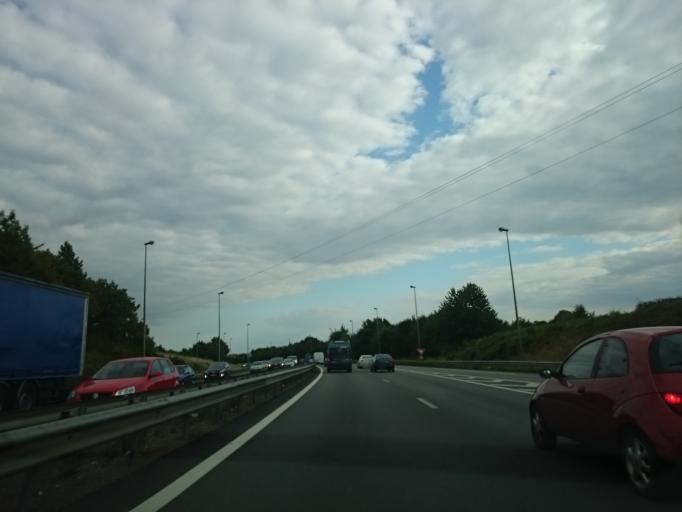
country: FR
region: Pays de la Loire
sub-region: Departement de la Loire-Atlantique
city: Saint-Herblain
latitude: 47.2098
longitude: -1.6269
